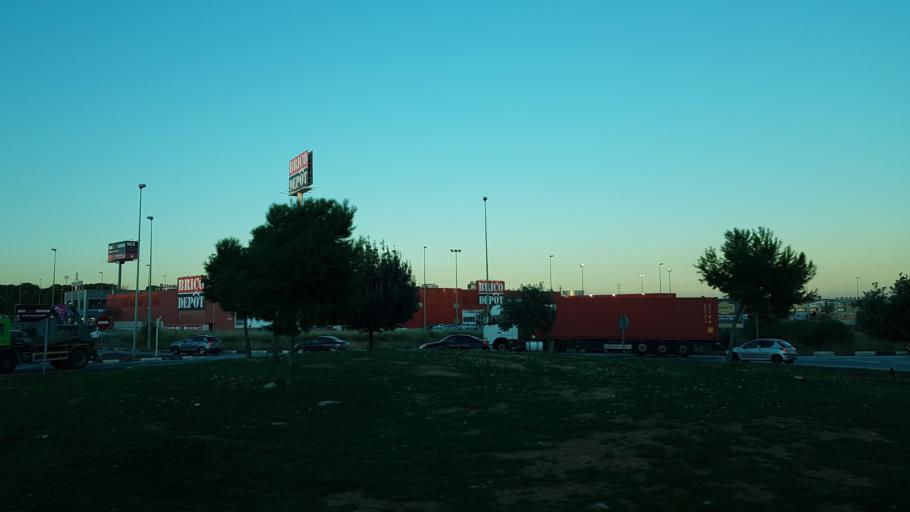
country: ES
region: Valencia
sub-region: Provincia de Valencia
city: Aldaia
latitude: 39.4744
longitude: -0.4821
